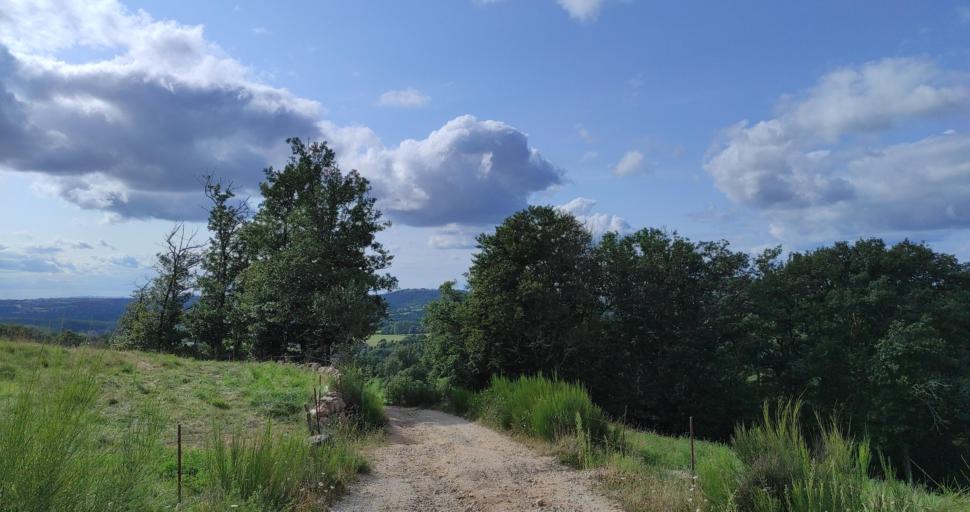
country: FR
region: Midi-Pyrenees
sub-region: Departement de l'Aveyron
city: La Loubiere
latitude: 44.3844
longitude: 2.7148
